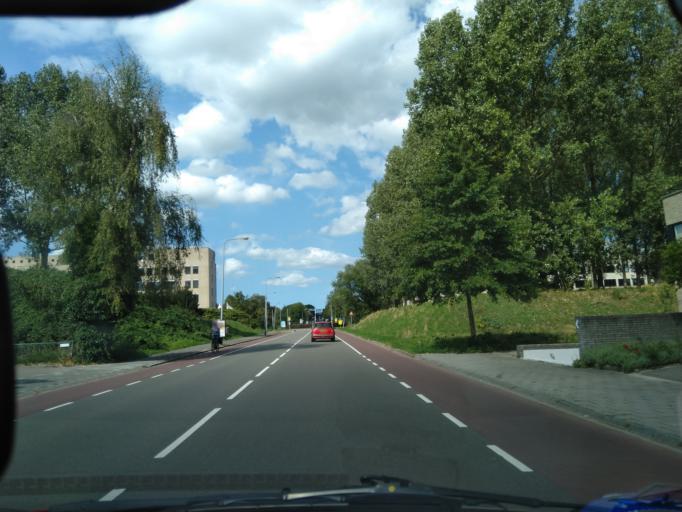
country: NL
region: Groningen
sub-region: Gemeente Groningen
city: Groningen
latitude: 53.1884
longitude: 6.5510
